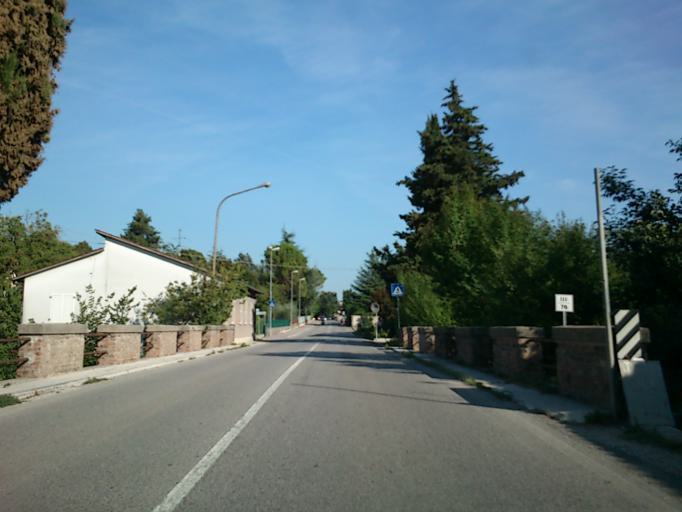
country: IT
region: The Marches
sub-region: Provincia di Pesaro e Urbino
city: Canavaccio
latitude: 43.6955
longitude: 12.6967
